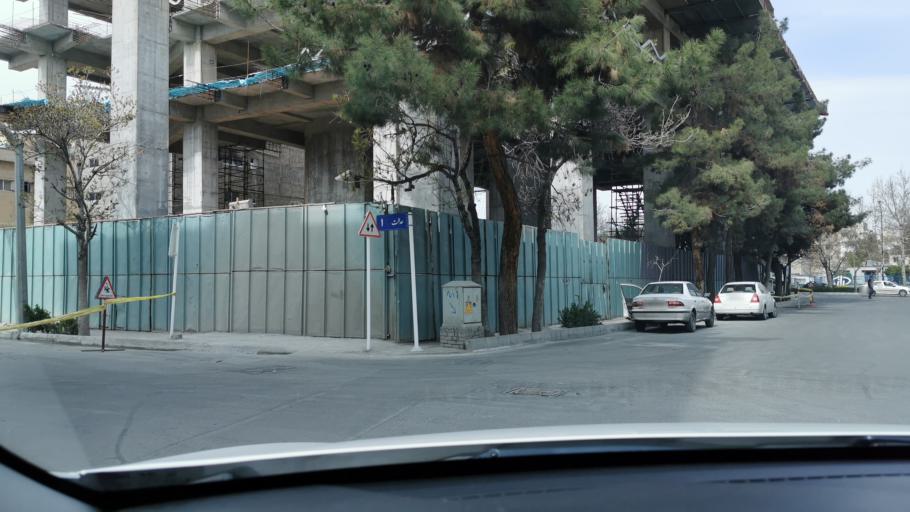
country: IR
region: Razavi Khorasan
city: Mashhad
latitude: 36.2950
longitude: 59.5754
